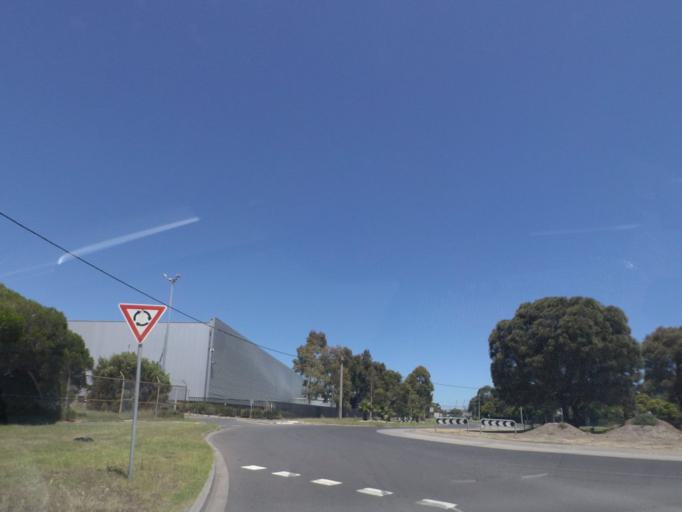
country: AU
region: Victoria
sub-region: Maribyrnong
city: Yarraville
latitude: -37.8265
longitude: 144.9118
